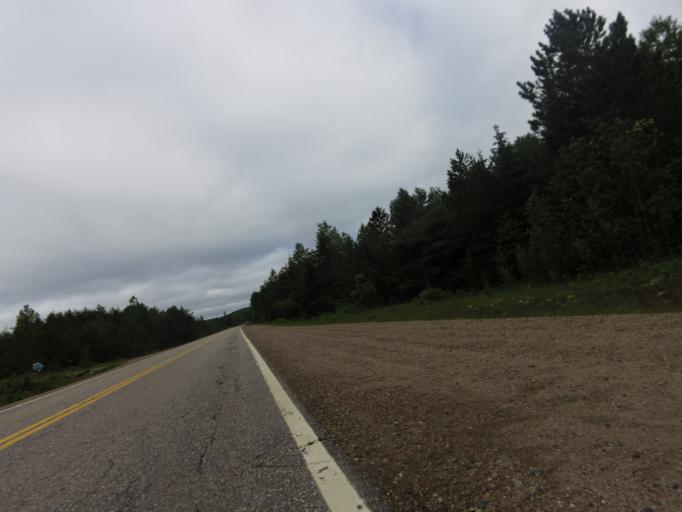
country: CA
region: Quebec
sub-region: Outaouais
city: Shawville
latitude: 45.9070
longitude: -76.3022
